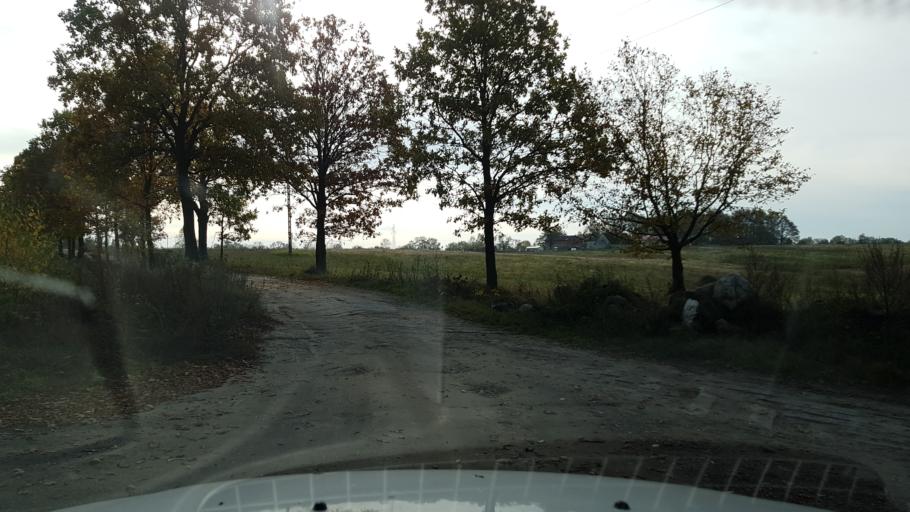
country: PL
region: West Pomeranian Voivodeship
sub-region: Powiat swidwinski
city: Polczyn-Zdroj
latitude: 53.7509
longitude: 16.0325
